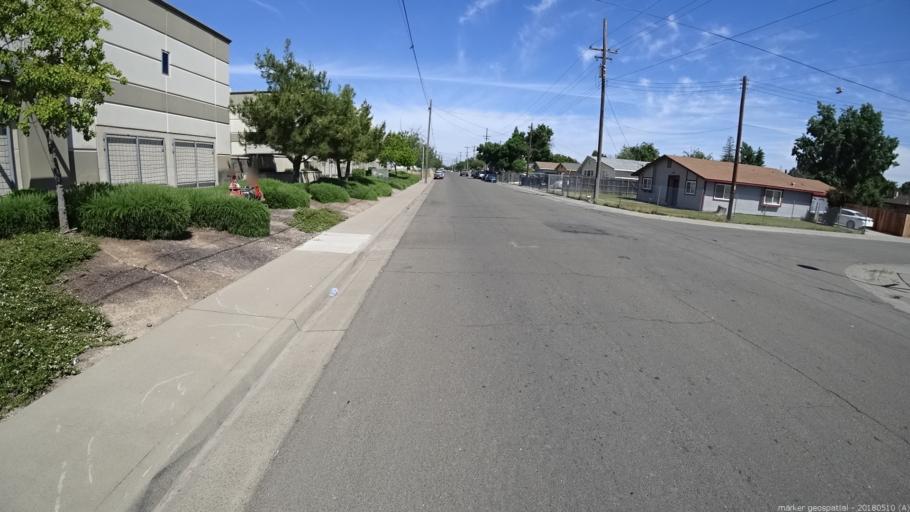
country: US
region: California
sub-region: Sacramento County
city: Rio Linda
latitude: 38.6387
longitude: -121.4551
